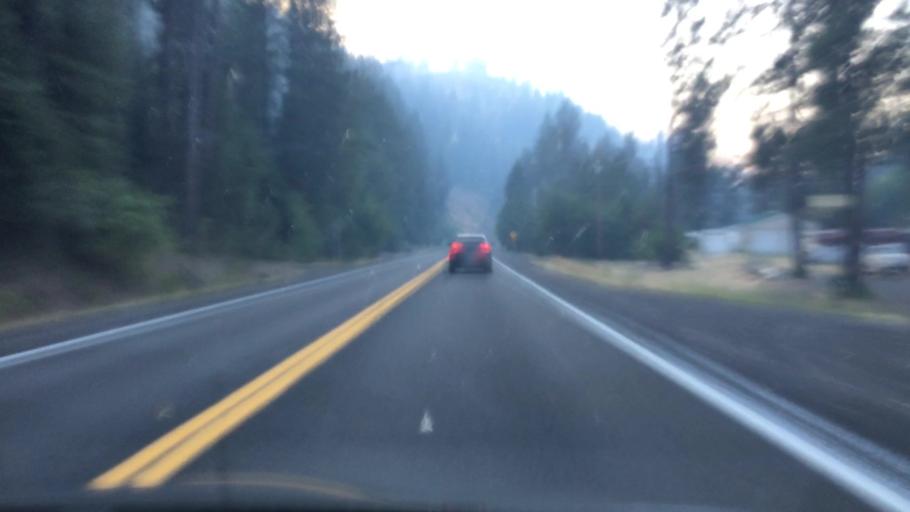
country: US
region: Idaho
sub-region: Valley County
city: McCall
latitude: 45.2279
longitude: -116.3228
